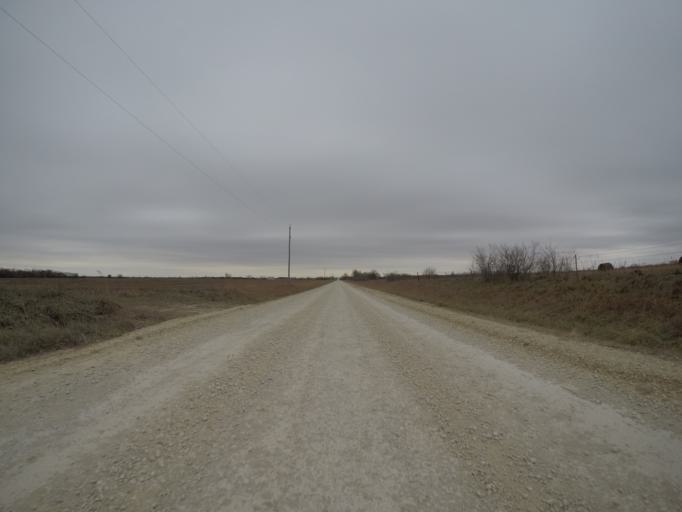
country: US
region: Kansas
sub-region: Wabaunsee County
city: Alma
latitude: 38.8444
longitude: -96.1133
